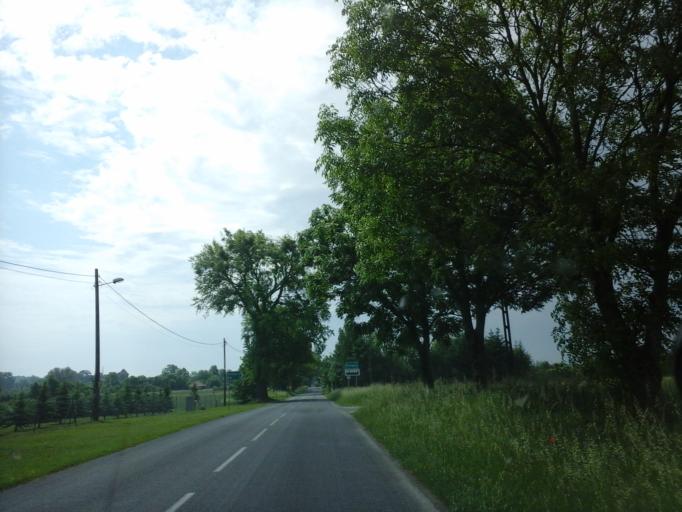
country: PL
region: West Pomeranian Voivodeship
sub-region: Powiat choszczenski
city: Drawno
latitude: 53.2268
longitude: 15.7525
